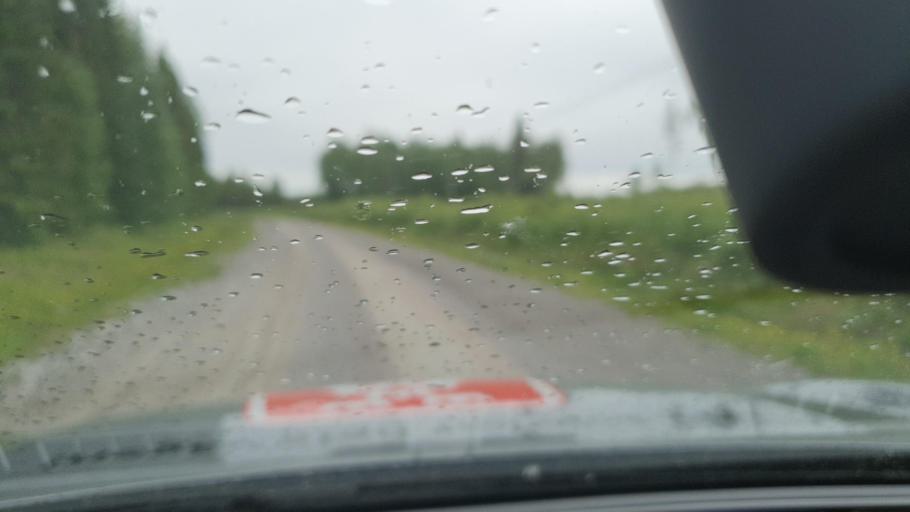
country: SE
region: Norrbotten
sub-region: Kalix Kommun
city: Rolfs
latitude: 66.0659
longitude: 22.9951
